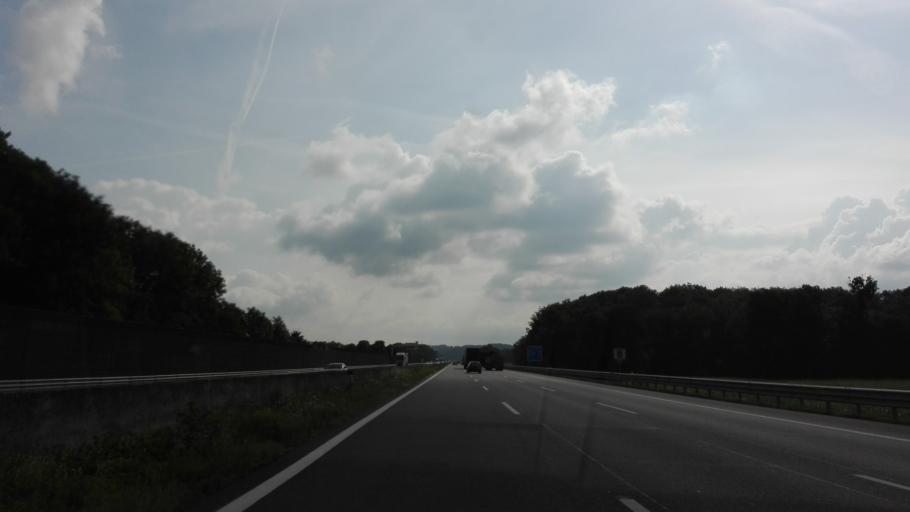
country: AT
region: Lower Austria
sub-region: Politischer Bezirk Melk
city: Neumarkt an der Ybbs
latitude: 48.1301
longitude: 15.0239
